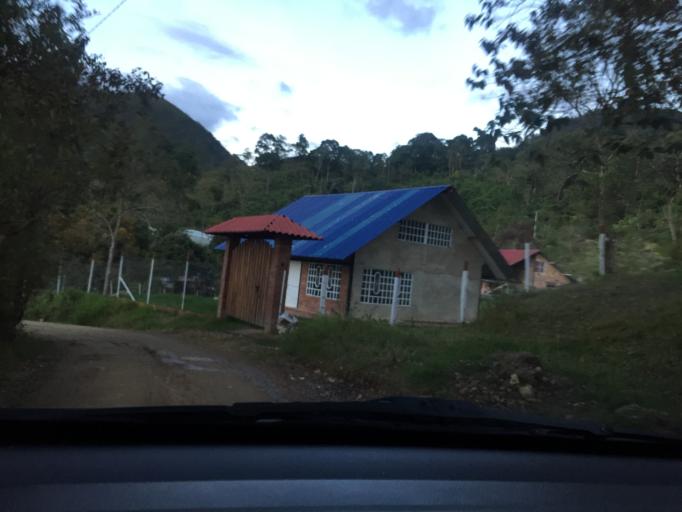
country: CO
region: Cundinamarca
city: Zipacon
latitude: 4.7064
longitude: -74.4088
